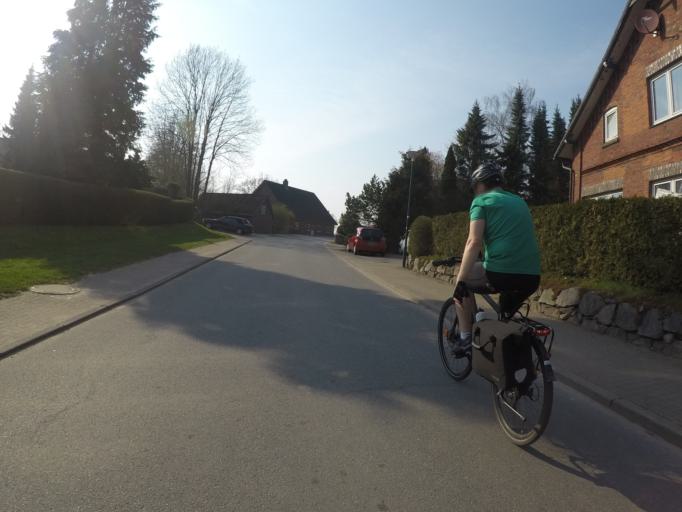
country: DE
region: Schleswig-Holstein
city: Leezen
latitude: 53.8708
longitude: 10.2462
